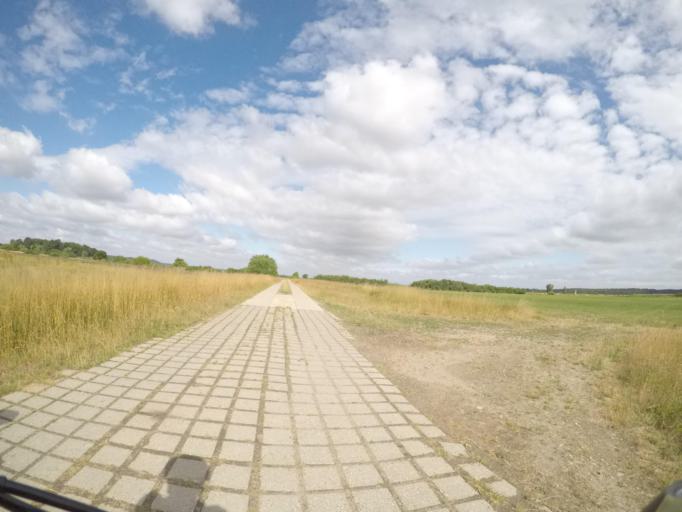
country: DE
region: Lower Saxony
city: Hitzacker
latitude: 53.1728
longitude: 11.0523
